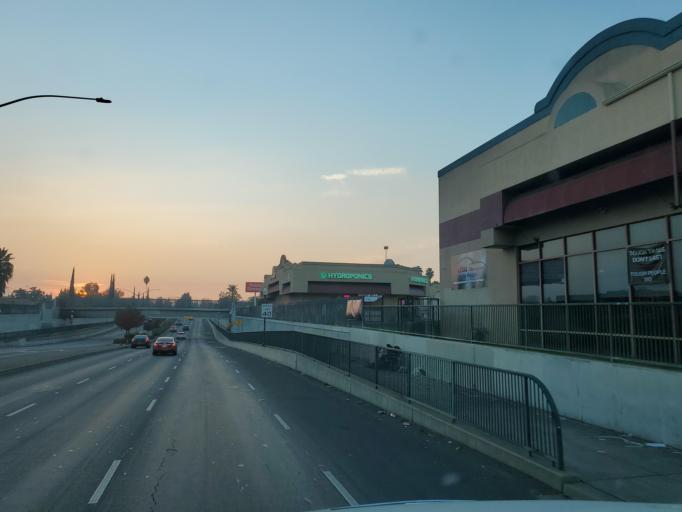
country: US
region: California
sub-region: San Joaquin County
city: Lincoln Village
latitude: 38.0017
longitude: -121.2928
